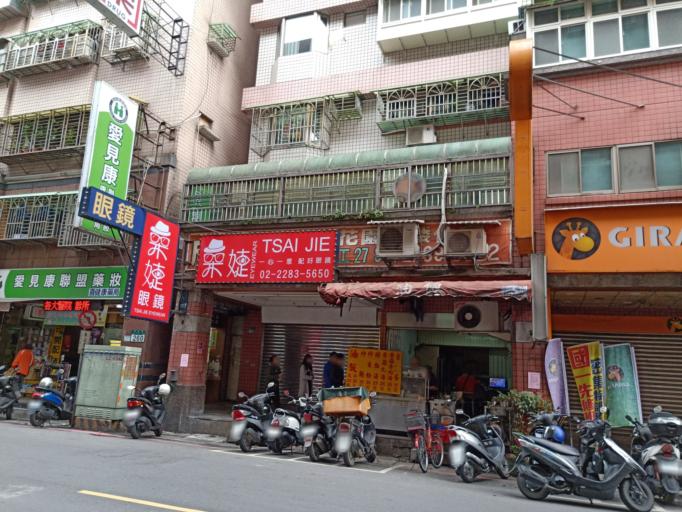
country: TW
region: Taipei
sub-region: Taipei
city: Banqiao
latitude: 25.0864
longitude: 121.4576
